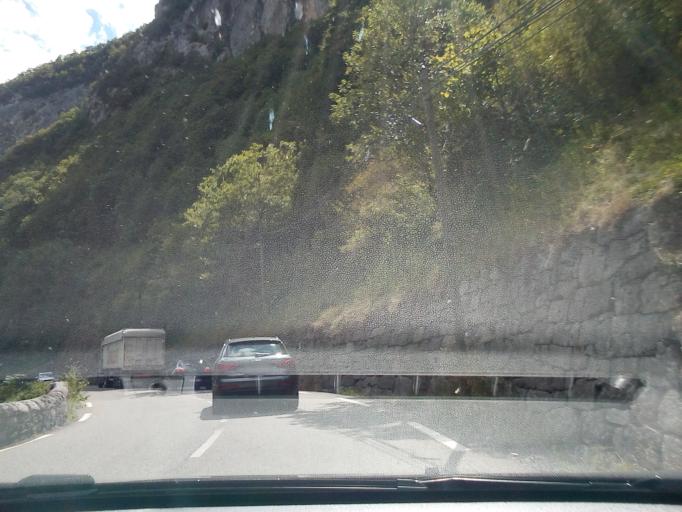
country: FR
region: Aquitaine
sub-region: Departement des Pyrenees-Atlantiques
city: Laruns
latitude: 42.8873
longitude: -0.5630
